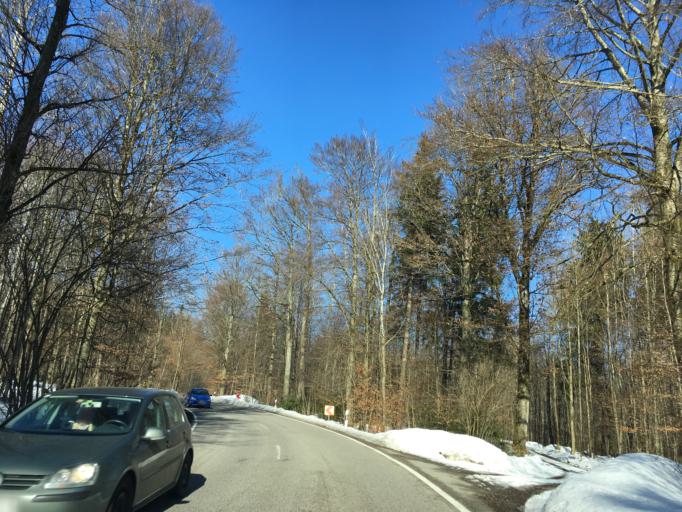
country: DE
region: Bavaria
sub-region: Upper Bavaria
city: Maitenbeth
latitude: 48.1249
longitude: 12.0877
